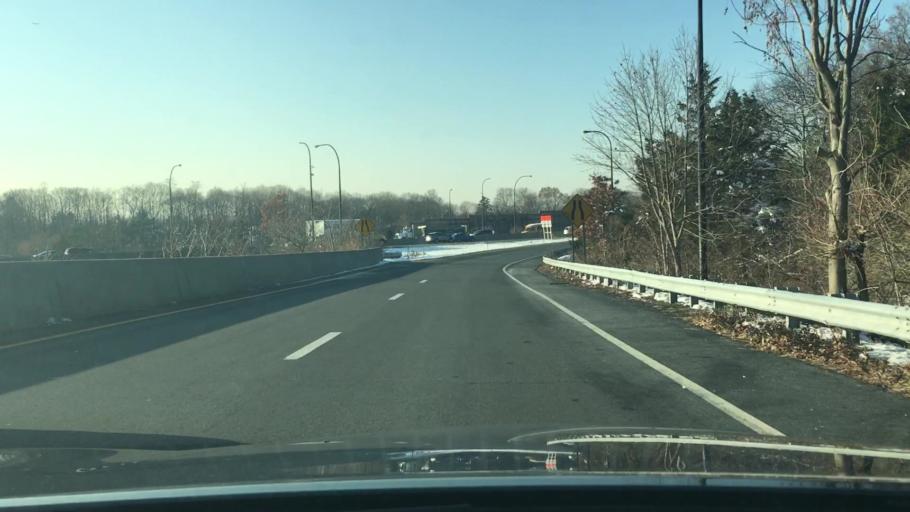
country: US
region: New York
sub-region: Nassau County
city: Syosset
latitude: 40.8004
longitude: -73.4909
